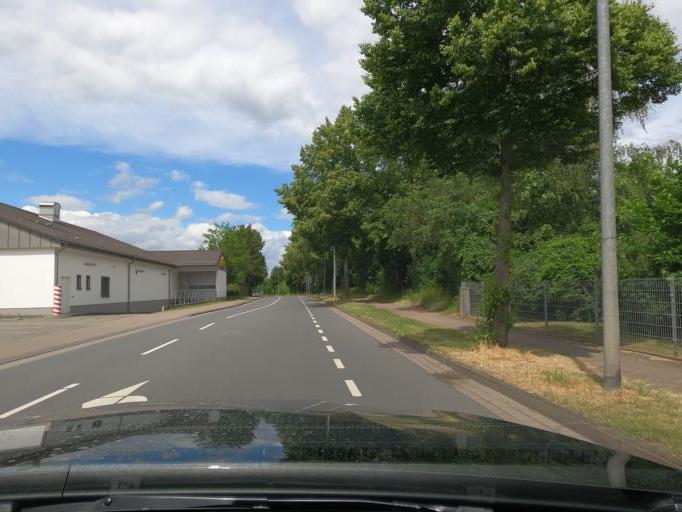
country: DE
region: Lower Saxony
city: Burgdorf
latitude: 52.4555
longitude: 9.9956
